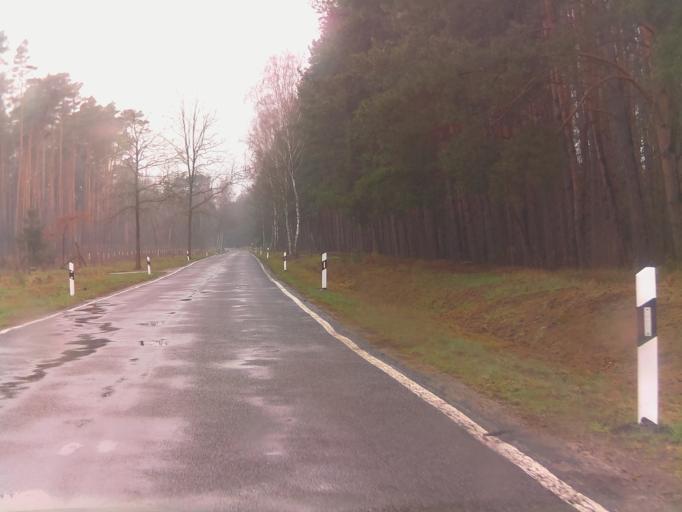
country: DE
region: Brandenburg
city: Jamlitz
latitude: 52.0328
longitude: 14.3276
